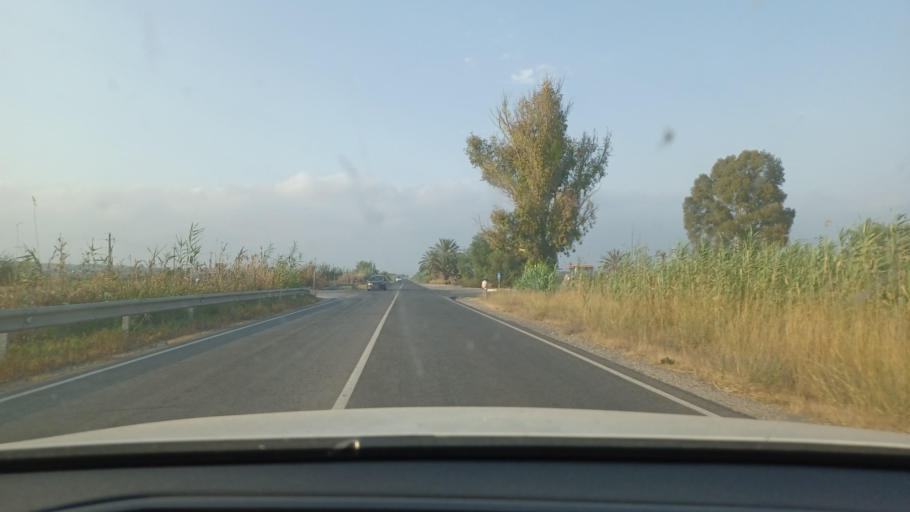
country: ES
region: Valencia
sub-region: Provincia de Alicante
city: Daya Vieja
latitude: 38.1672
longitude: -0.7026
